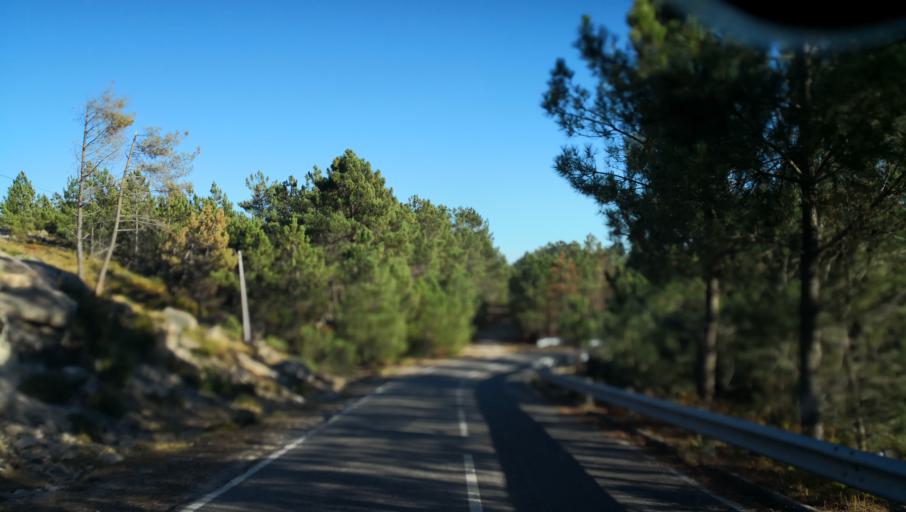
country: PT
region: Vila Real
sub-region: Vila Real
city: Vila Real
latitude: 41.3390
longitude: -7.7878
